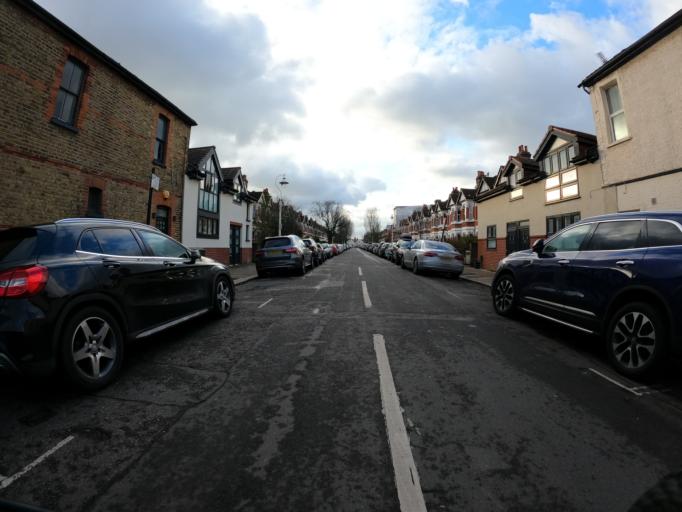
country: GB
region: England
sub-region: Greater London
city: Ealing
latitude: 51.5021
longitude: -0.3163
